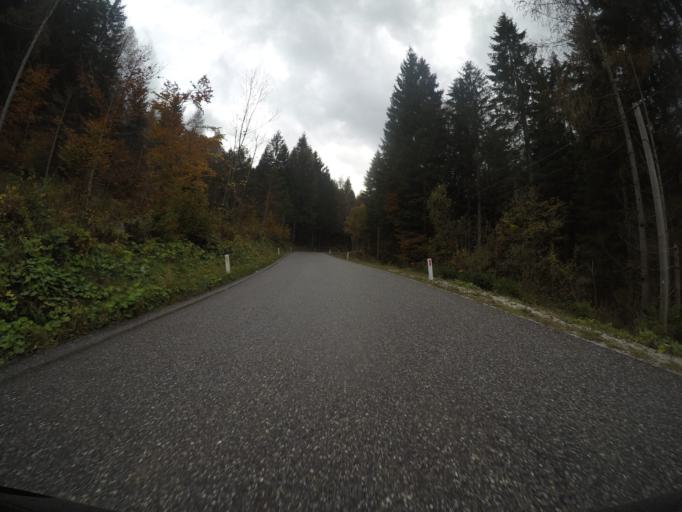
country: SI
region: Kranjska Gora
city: Mojstrana
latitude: 46.4509
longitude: 13.9356
